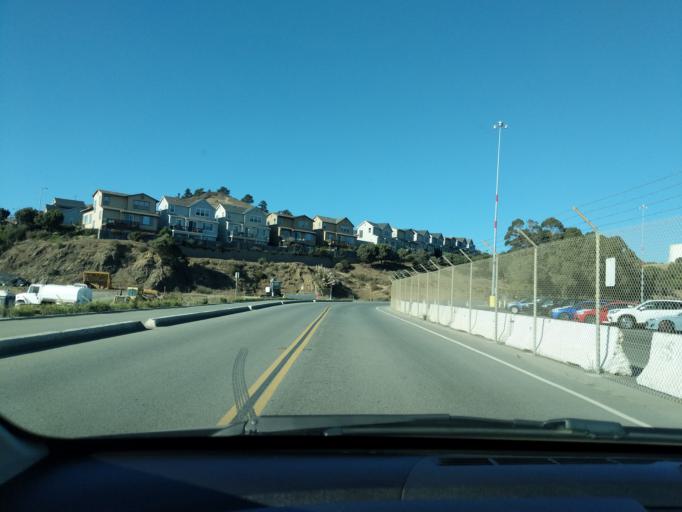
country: US
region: California
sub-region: Contra Costa County
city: Richmond
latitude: 37.9087
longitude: -122.3730
